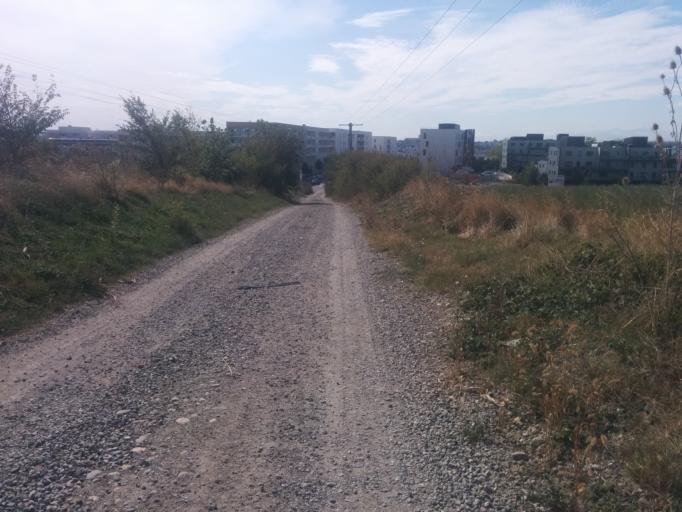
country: FR
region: Midi-Pyrenees
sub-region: Departement de la Haute-Garonne
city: Balma
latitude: 43.6264
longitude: 1.4974
